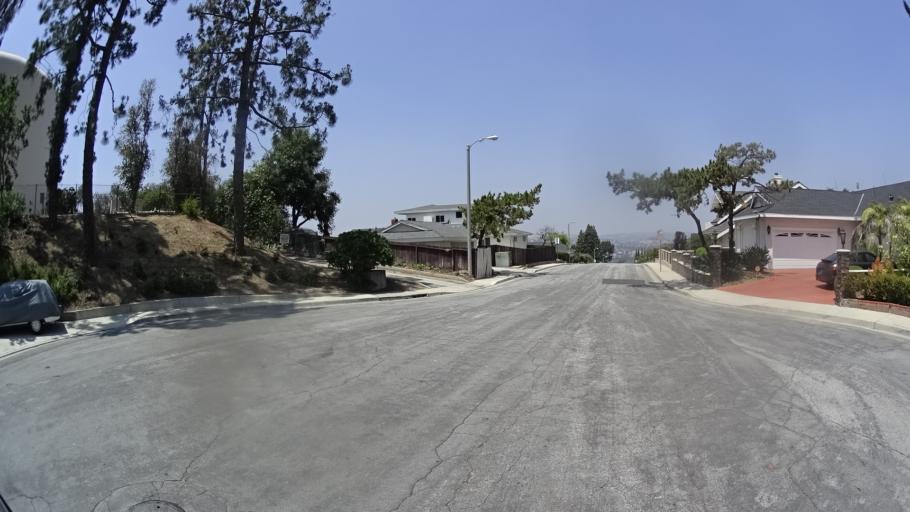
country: US
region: California
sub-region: Los Angeles County
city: Monterey Park
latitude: 34.0594
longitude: -118.1480
